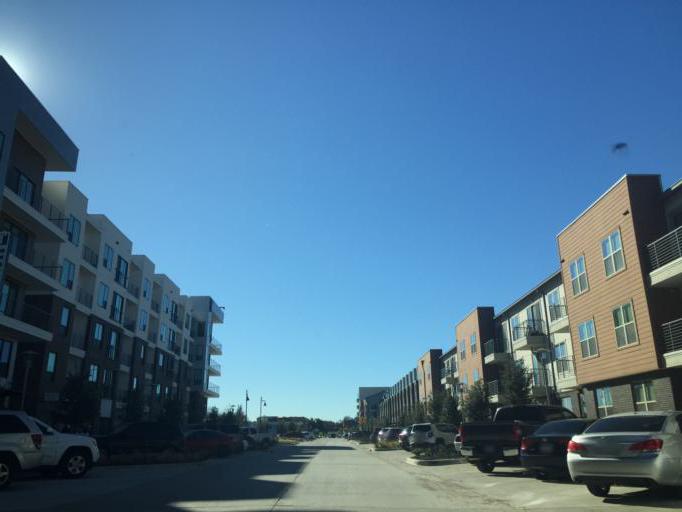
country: US
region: Texas
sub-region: Tarrant County
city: Fort Worth
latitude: 32.7550
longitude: -97.3489
